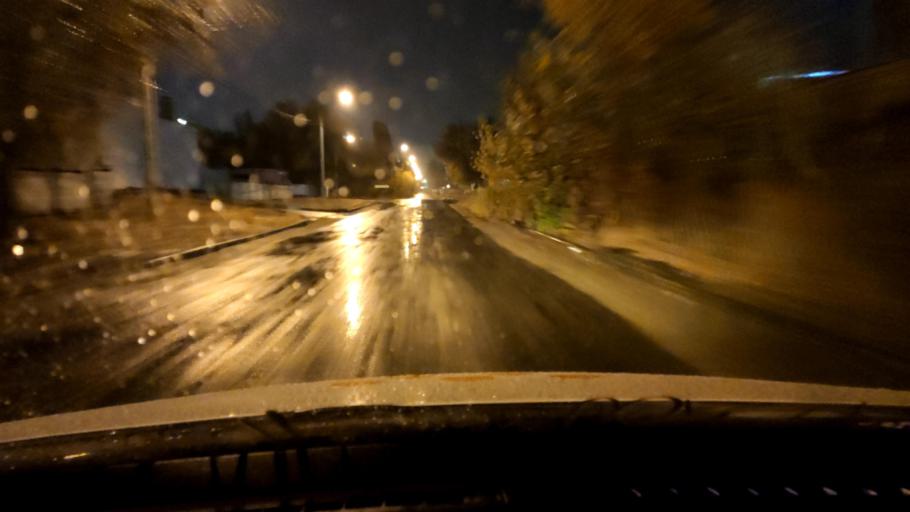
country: RU
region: Voronezj
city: Voronezh
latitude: 51.6439
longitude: 39.1267
